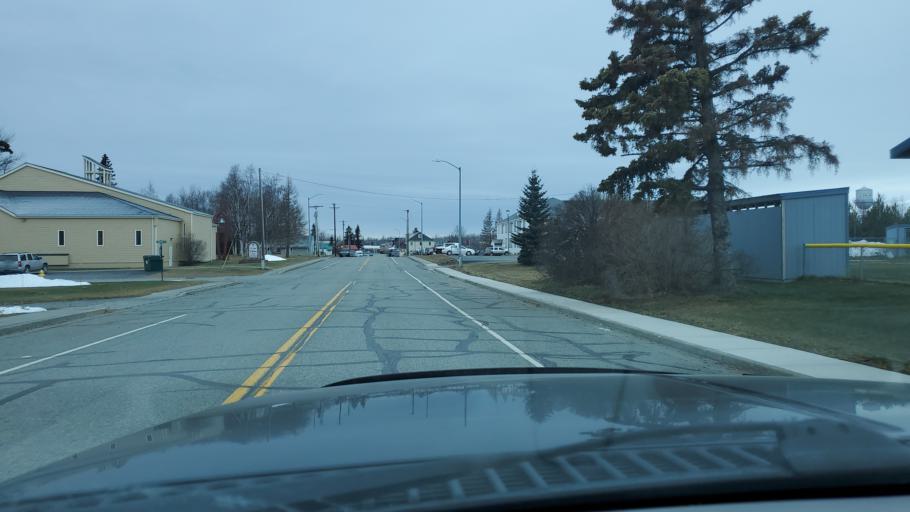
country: US
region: Alaska
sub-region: Matanuska-Susitna Borough
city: Palmer
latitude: 61.5988
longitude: -149.1052
